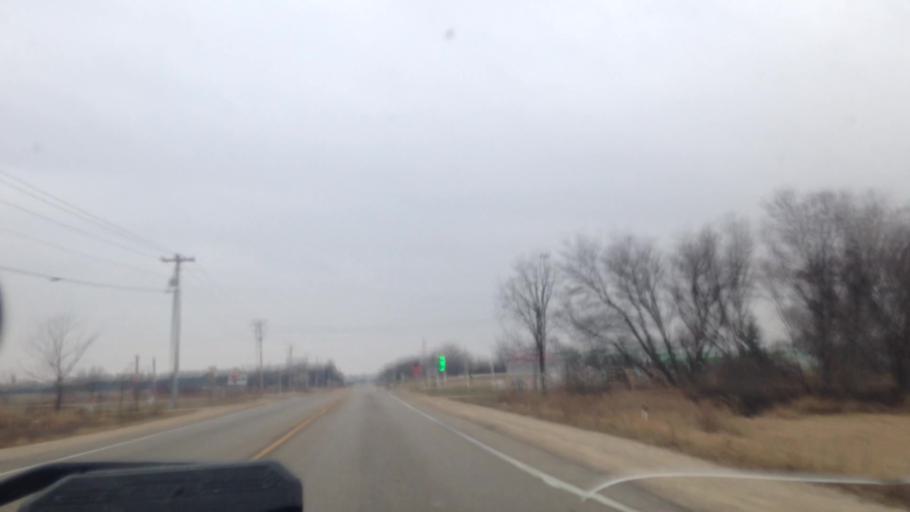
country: US
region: Wisconsin
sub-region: Dodge County
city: Juneau
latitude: 43.4435
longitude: -88.6927
